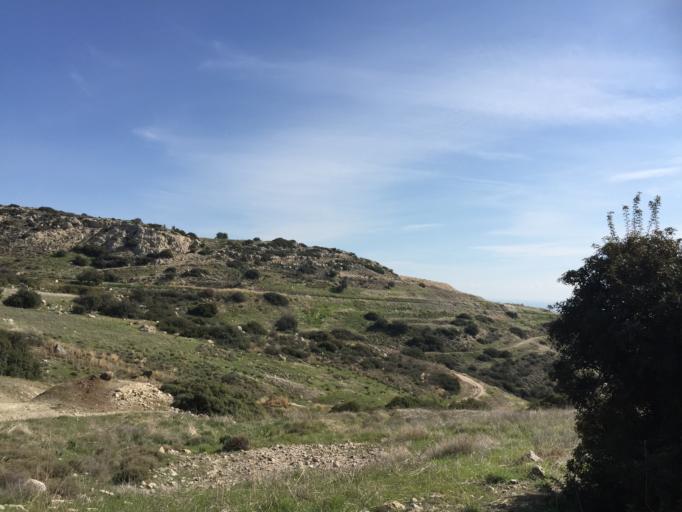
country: CY
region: Larnaka
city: Agios Tychon
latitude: 34.7393
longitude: 33.1252
